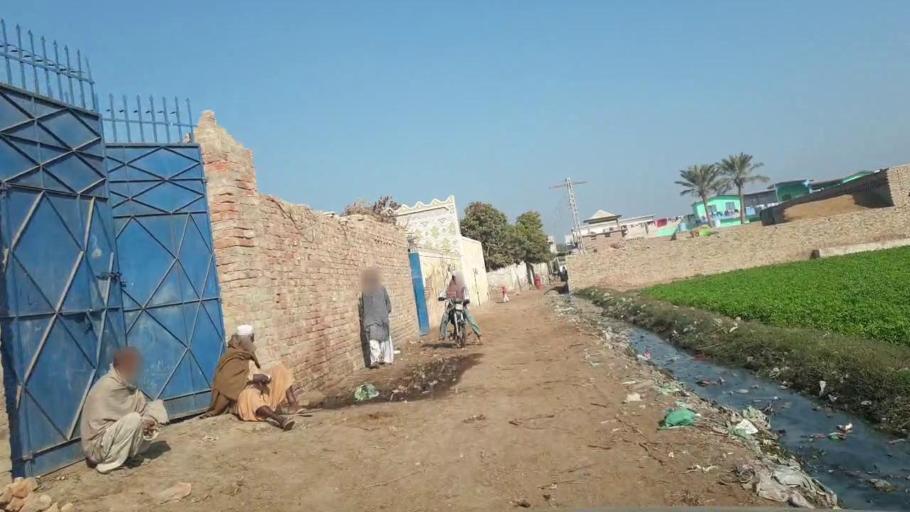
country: PK
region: Sindh
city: Shahdadpur
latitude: 25.9454
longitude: 68.5924
